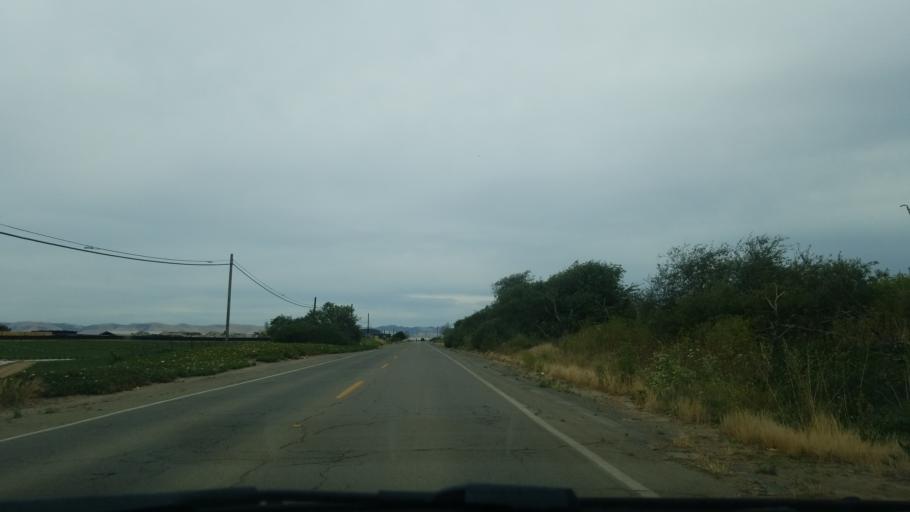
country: US
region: California
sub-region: Santa Barbara County
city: Santa Maria
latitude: 34.9156
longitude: -120.4822
